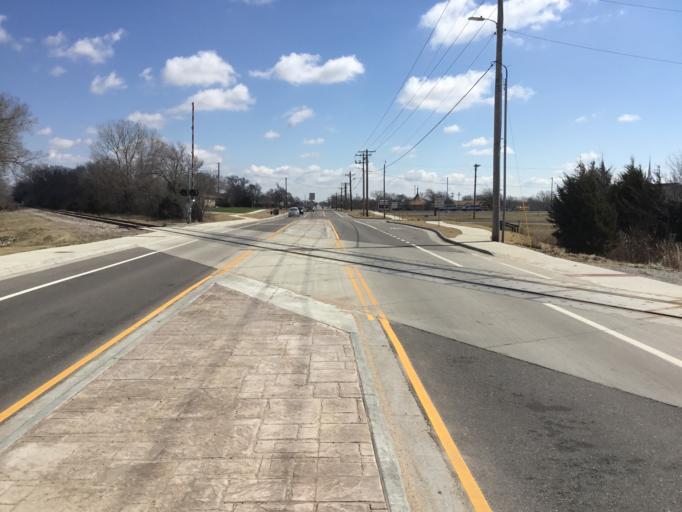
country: US
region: Kansas
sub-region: Sedgwick County
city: Bellaire
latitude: 37.7522
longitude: -97.2739
